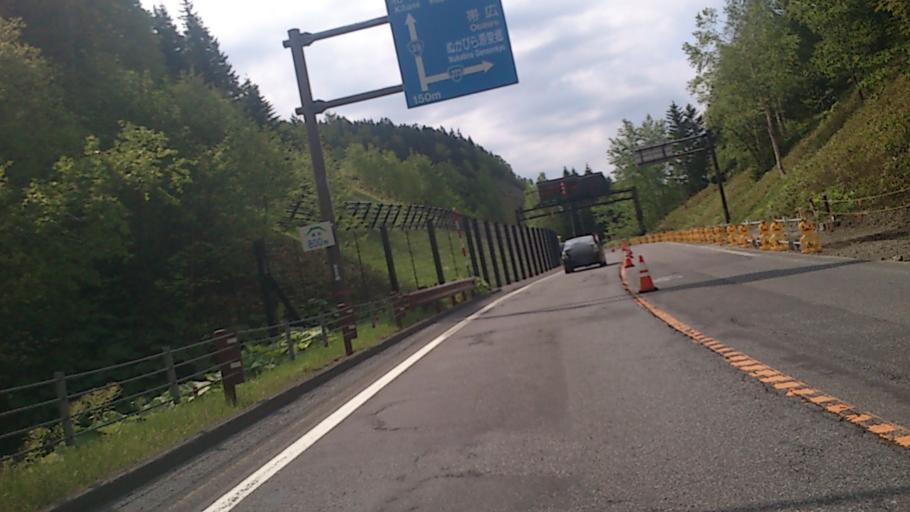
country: JP
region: Hokkaido
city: Kamikawa
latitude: 43.6825
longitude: 143.0351
